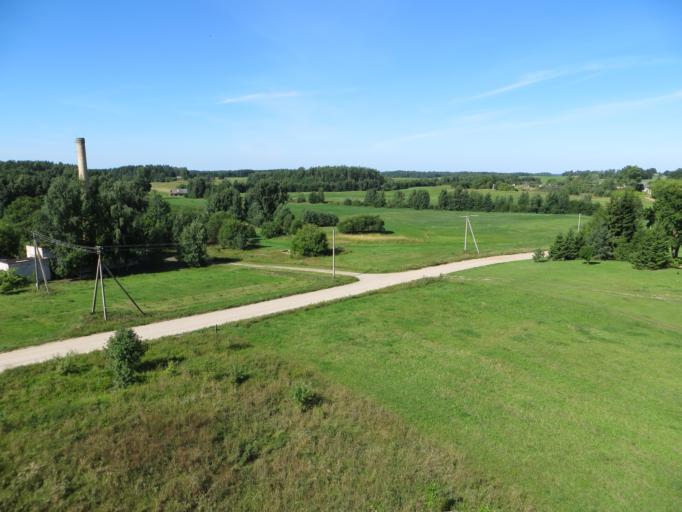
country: LT
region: Utenos apskritis
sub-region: Utena
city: Utena
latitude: 55.5868
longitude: 25.6727
